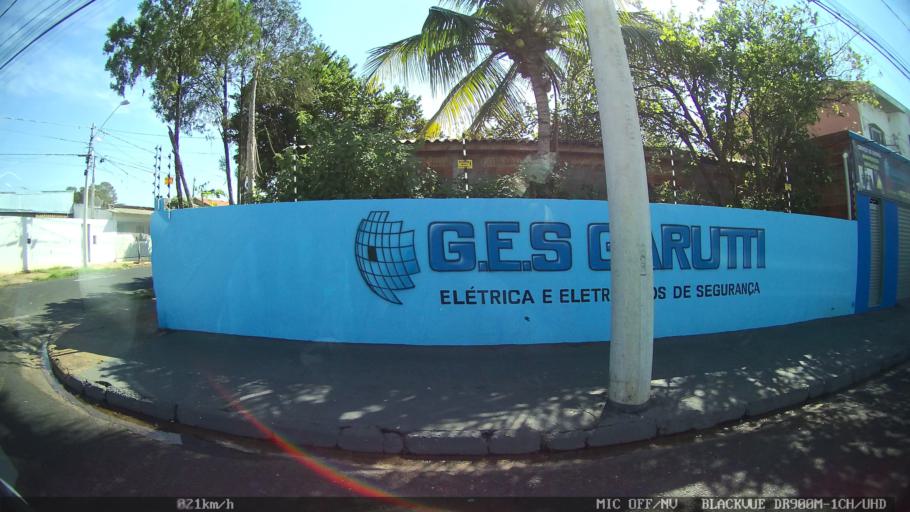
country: BR
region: Sao Paulo
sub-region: Sao Jose Do Rio Preto
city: Sao Jose do Rio Preto
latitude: -20.7790
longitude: -49.4068
